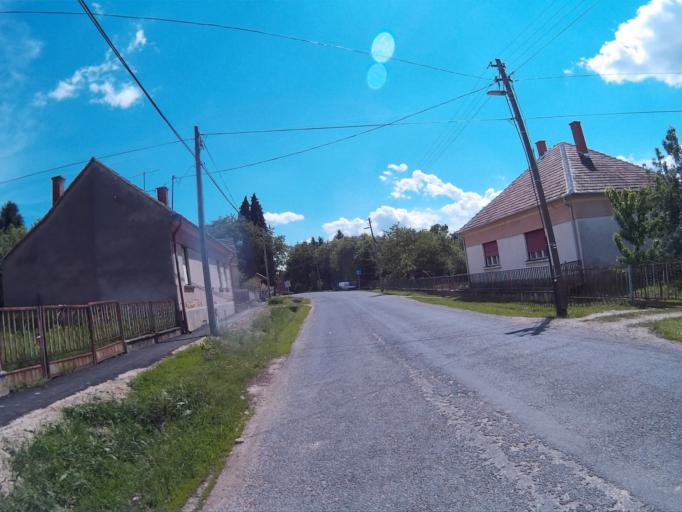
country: HU
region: Vas
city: Kormend
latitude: 46.9383
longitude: 16.5201
